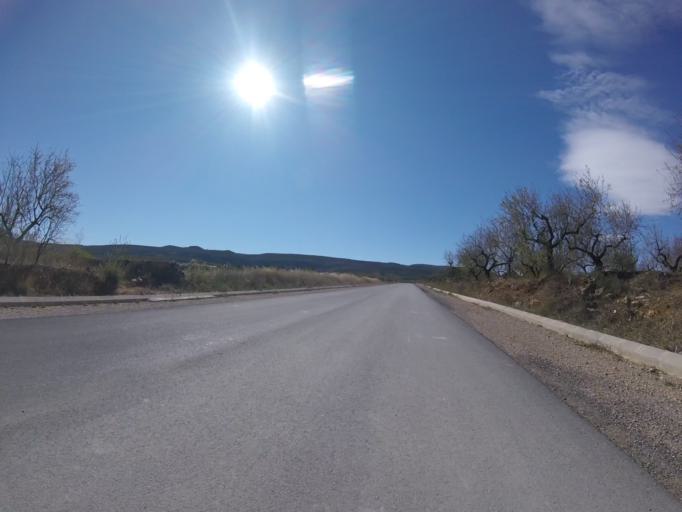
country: ES
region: Valencia
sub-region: Provincia de Castello
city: Albocasser
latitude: 40.3576
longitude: 0.0179
